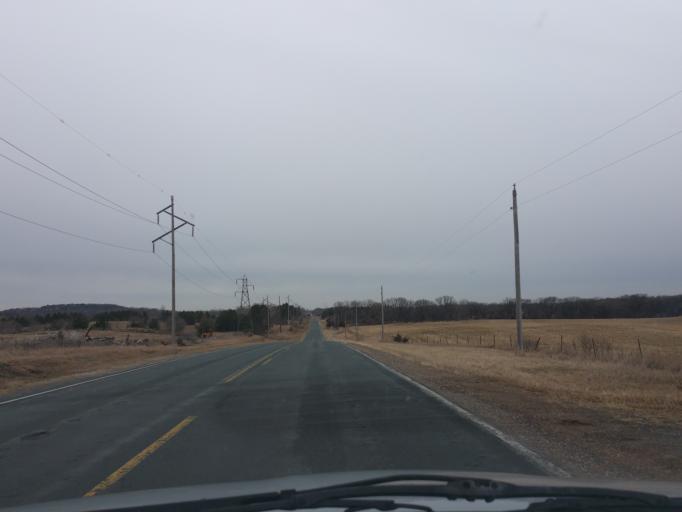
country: US
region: Wisconsin
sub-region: Saint Croix County
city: Roberts
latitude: 45.0357
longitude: -92.6090
